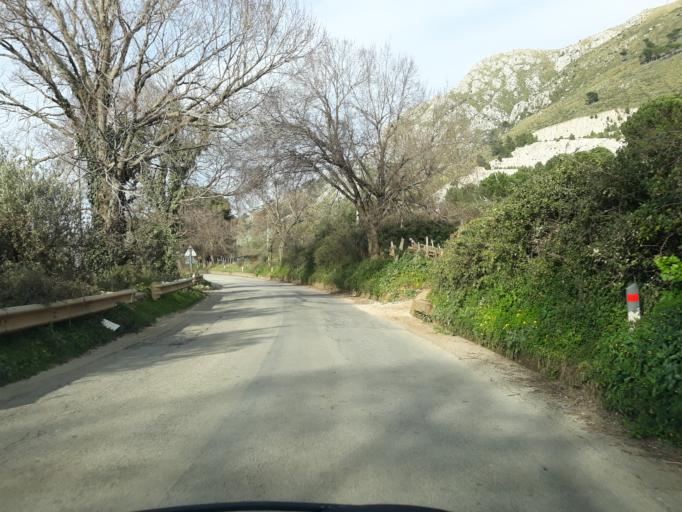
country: IT
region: Sicily
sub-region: Palermo
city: Torretta
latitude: 38.1074
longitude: 13.2352
